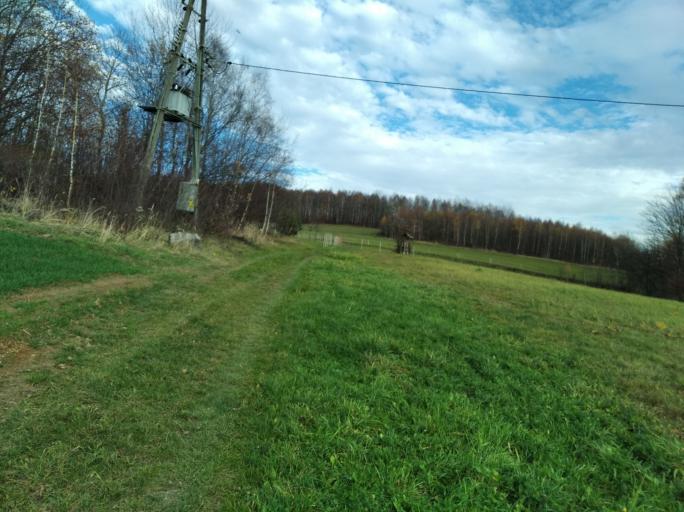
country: PL
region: Subcarpathian Voivodeship
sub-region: Powiat strzyzowski
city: Jawornik
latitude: 49.8492
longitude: 21.8479
